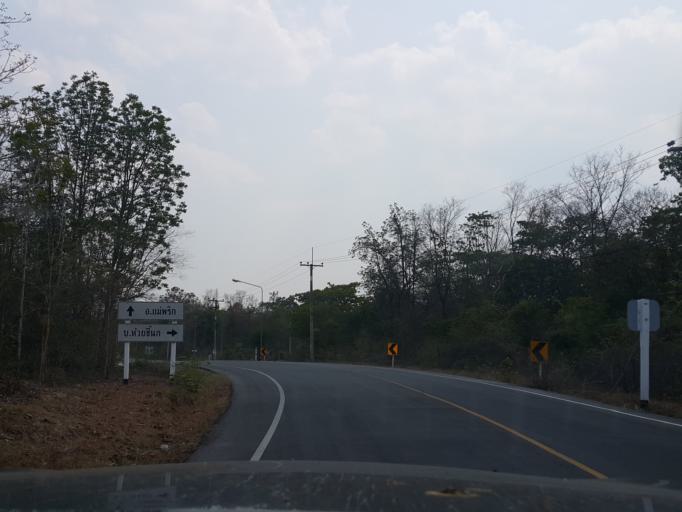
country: TH
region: Lampang
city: Mae Phrik
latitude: 17.4810
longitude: 99.1171
